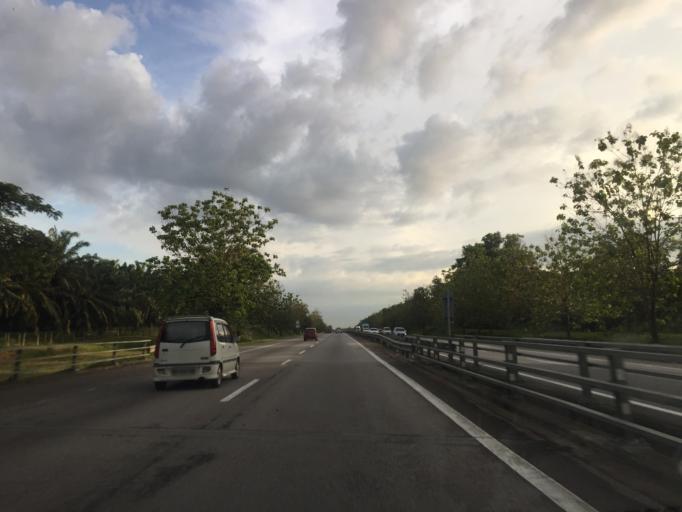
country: MY
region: Kedah
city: Bedong
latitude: 5.7754
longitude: 100.5035
